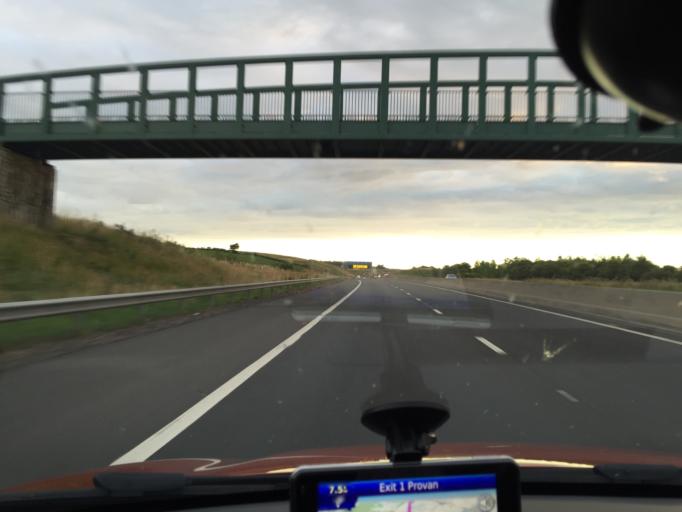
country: GB
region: Scotland
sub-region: North Lanarkshire
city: Chryston
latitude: 55.9164
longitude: -4.1078
